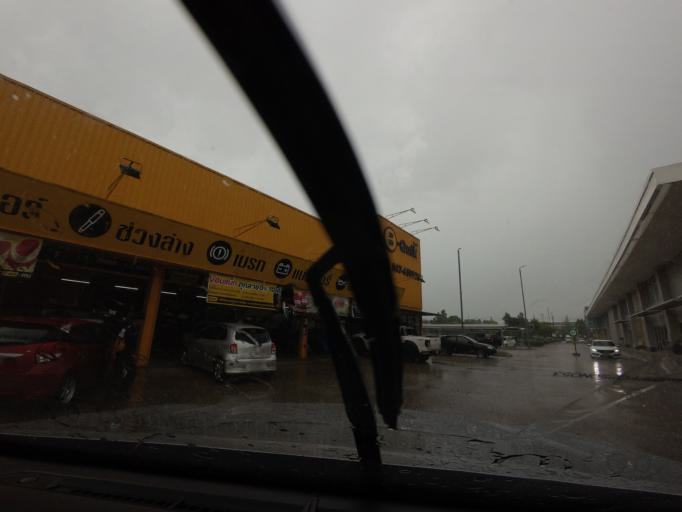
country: TH
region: Chumphon
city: Chumphon
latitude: 10.5030
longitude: 99.1392
